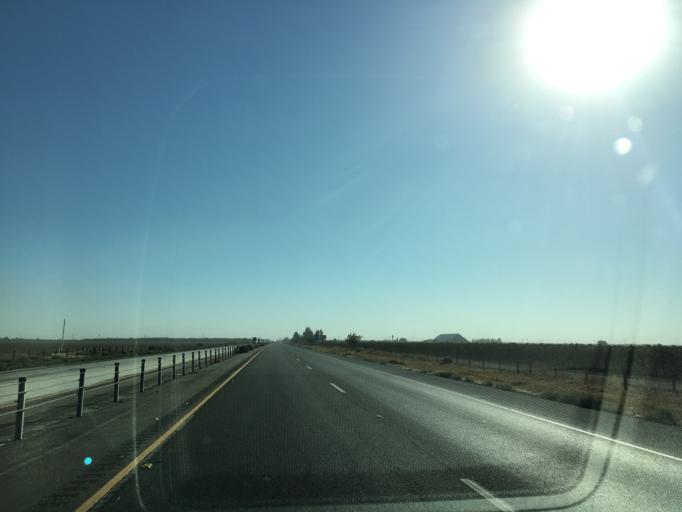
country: US
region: California
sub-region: Merced County
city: Dos Palos
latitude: 37.0836
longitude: -120.4879
